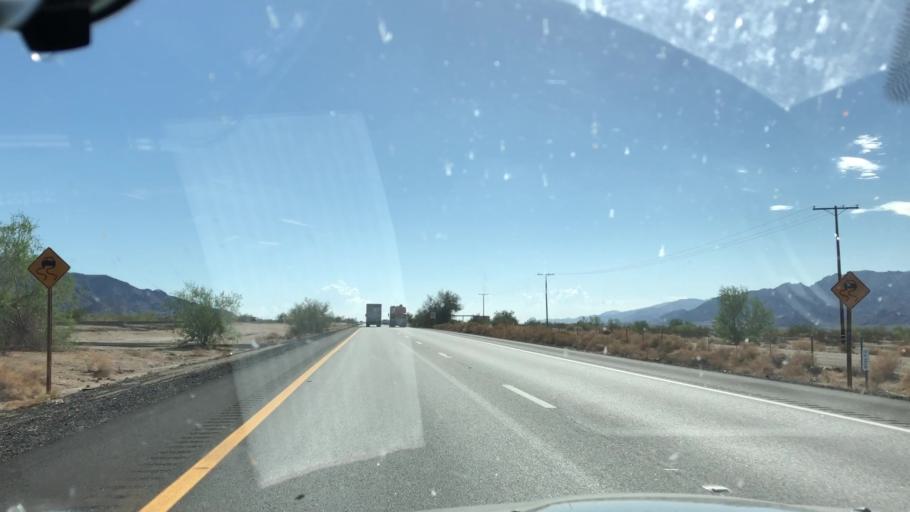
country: US
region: California
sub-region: Imperial County
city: Niland
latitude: 33.7060
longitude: -115.4359
